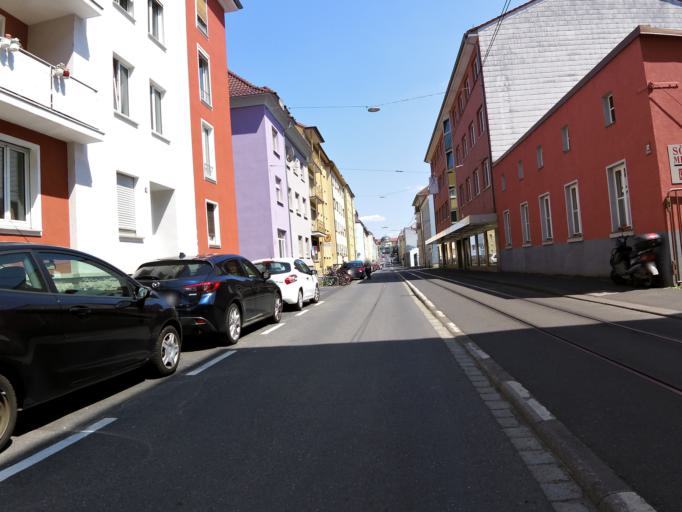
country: DE
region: Bavaria
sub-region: Regierungsbezirk Unterfranken
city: Wuerzburg
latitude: 49.8018
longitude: 9.9468
